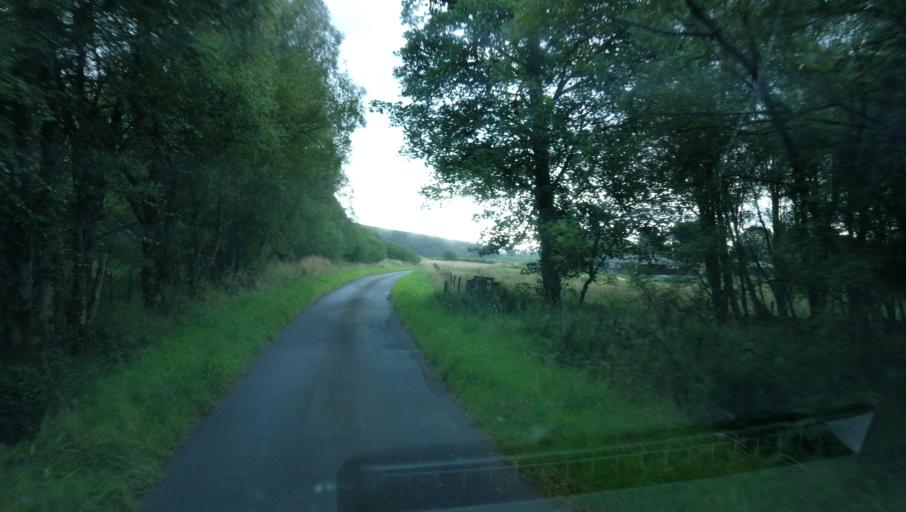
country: GB
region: Scotland
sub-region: Perth and Kinross
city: Blairgowrie
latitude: 56.6594
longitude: -3.3123
